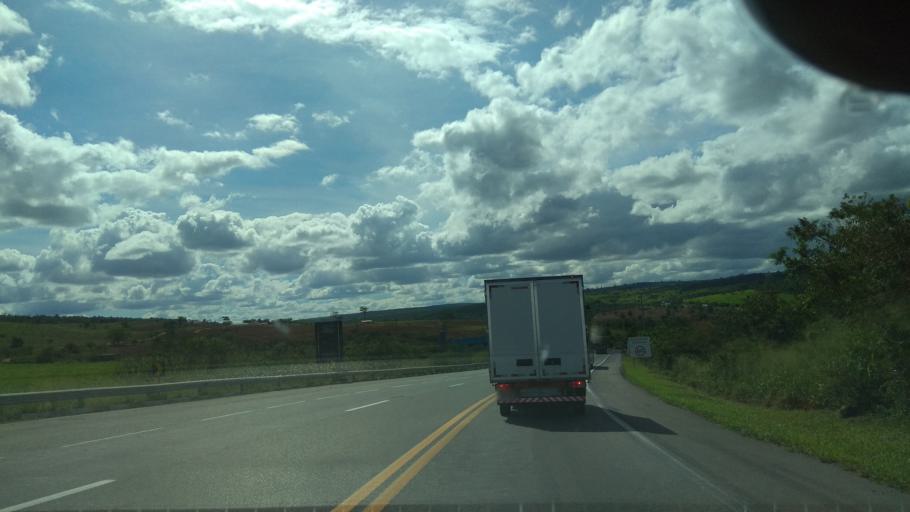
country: BR
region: Bahia
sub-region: Santa Ines
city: Santa Ines
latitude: -13.1644
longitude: -39.9993
